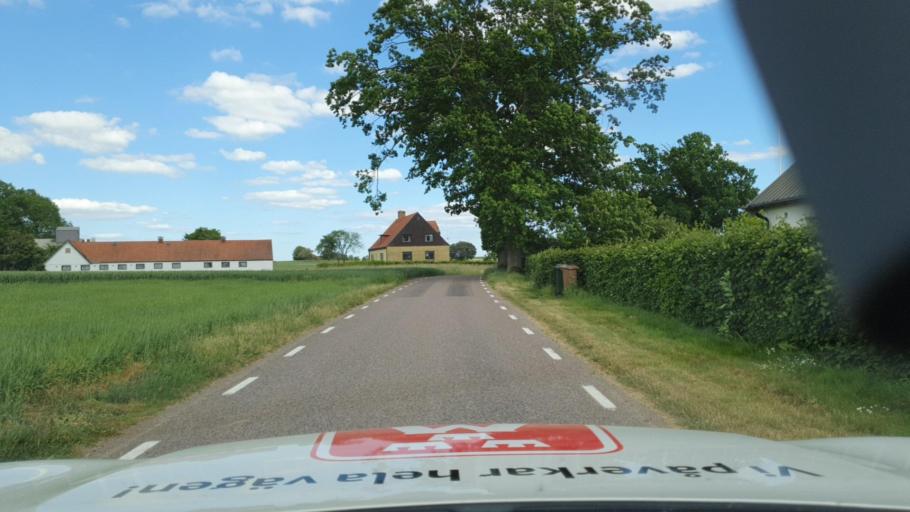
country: SE
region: Skane
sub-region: Ystads Kommun
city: Kopingebro
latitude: 55.4657
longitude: 13.9982
